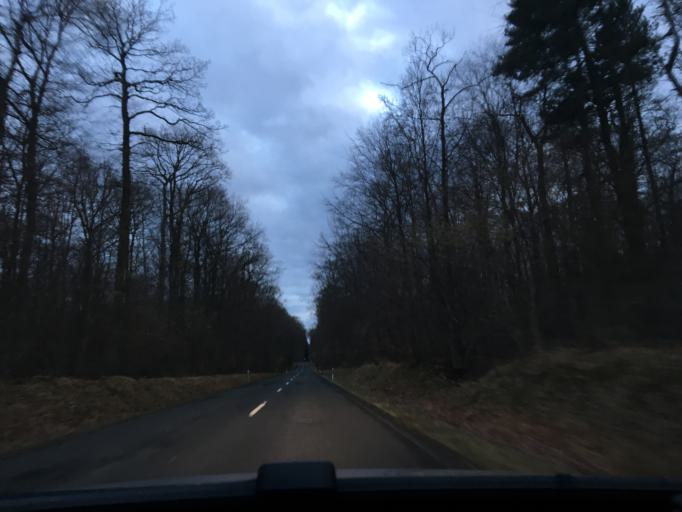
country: DE
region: Rheinland-Pfalz
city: Orbis
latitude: 49.7141
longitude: 8.0027
